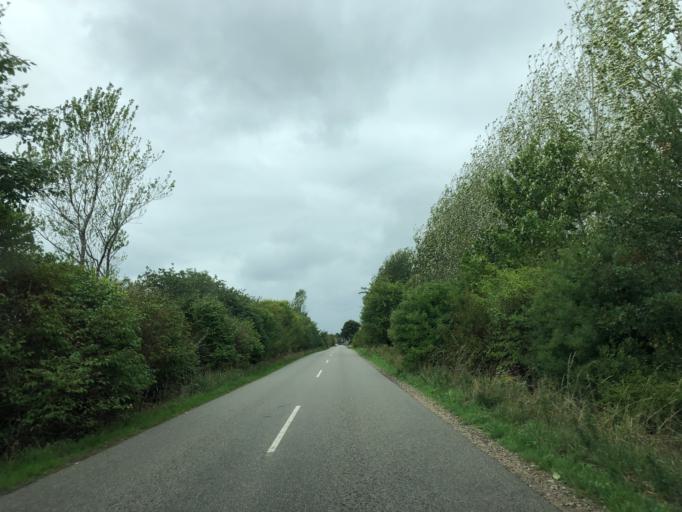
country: DK
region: Central Jutland
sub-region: Herning Kommune
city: Snejbjerg
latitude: 56.0914
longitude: 8.9206
